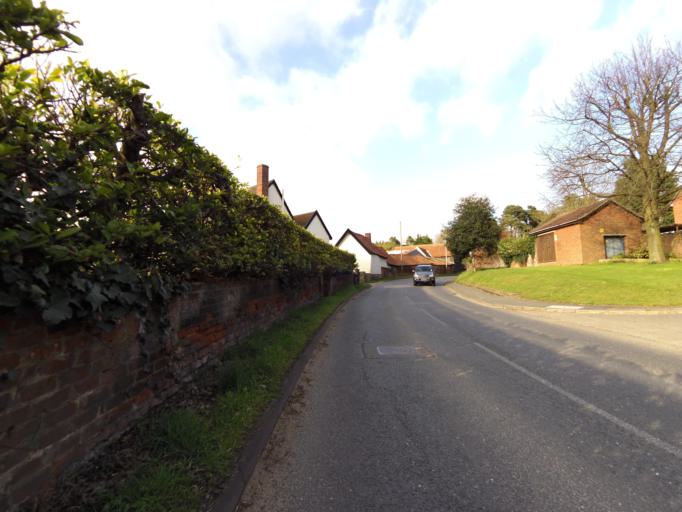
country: GB
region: England
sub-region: Suffolk
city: Kesgrave
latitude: 52.0925
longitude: 1.2009
